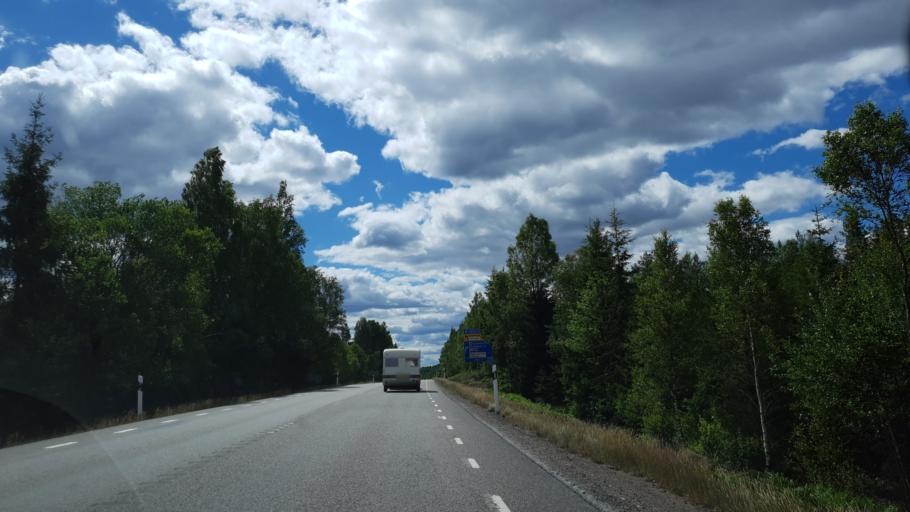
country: SE
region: Kronoberg
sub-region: Vaxjo Kommun
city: Braas
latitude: 57.1341
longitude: 15.1721
